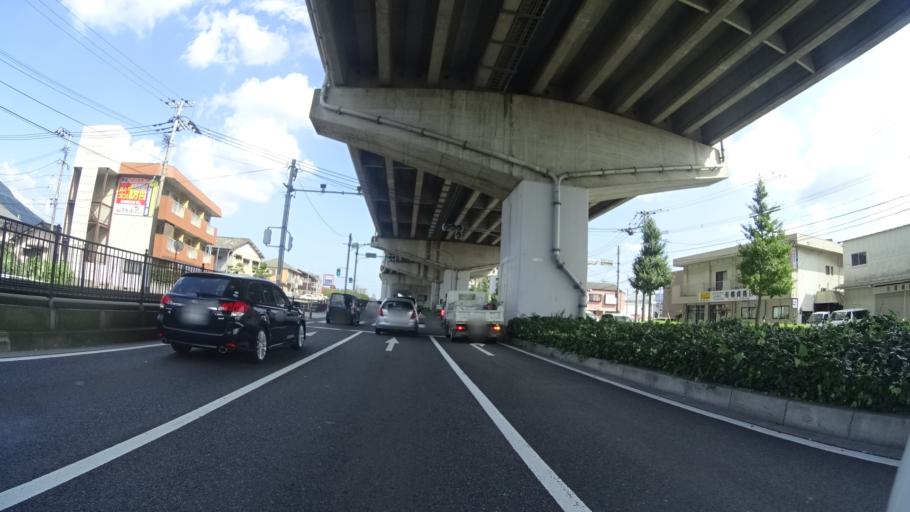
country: JP
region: Fukuoka
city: Kitakyushu
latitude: 33.8402
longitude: 130.8965
